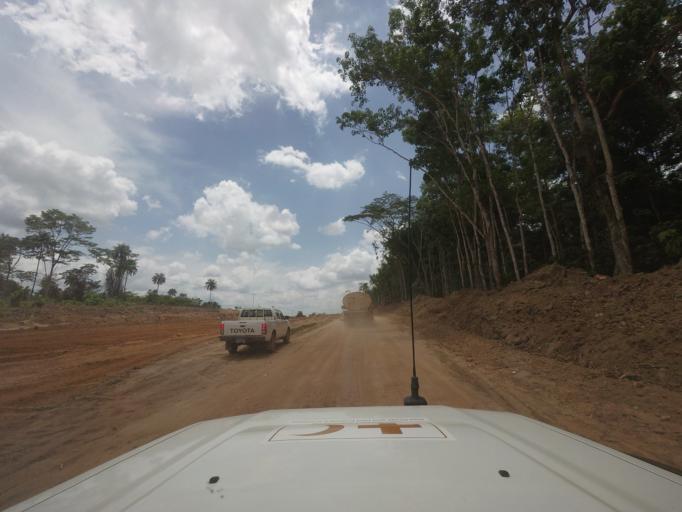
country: LR
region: Nimba
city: Sanniquellie
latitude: 7.2458
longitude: -8.8650
